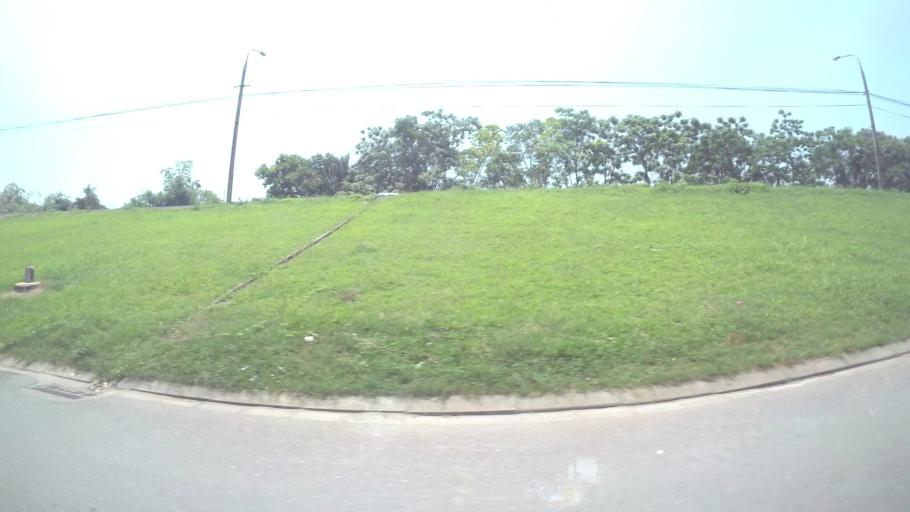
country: VN
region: Ha Noi
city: Hoan Kiem
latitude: 21.0240
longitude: 105.8862
